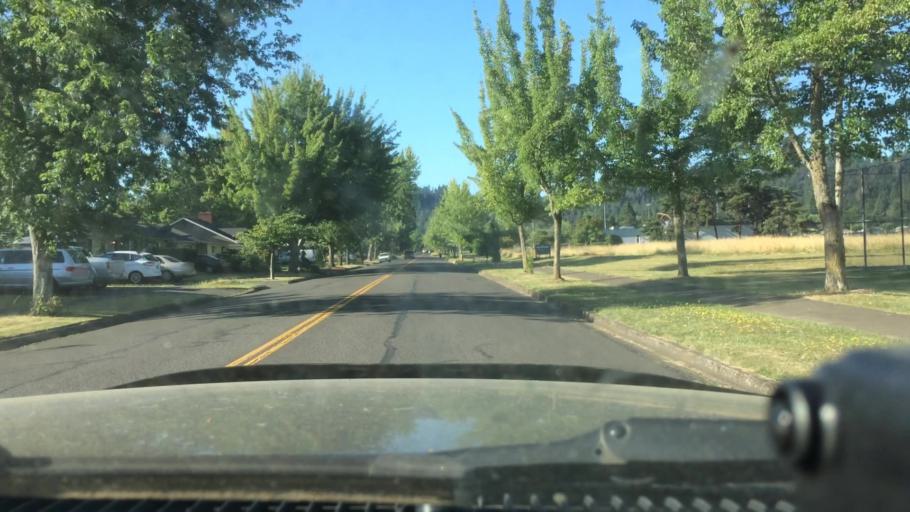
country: US
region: Oregon
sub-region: Lane County
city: Eugene
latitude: 44.0377
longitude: -123.1123
